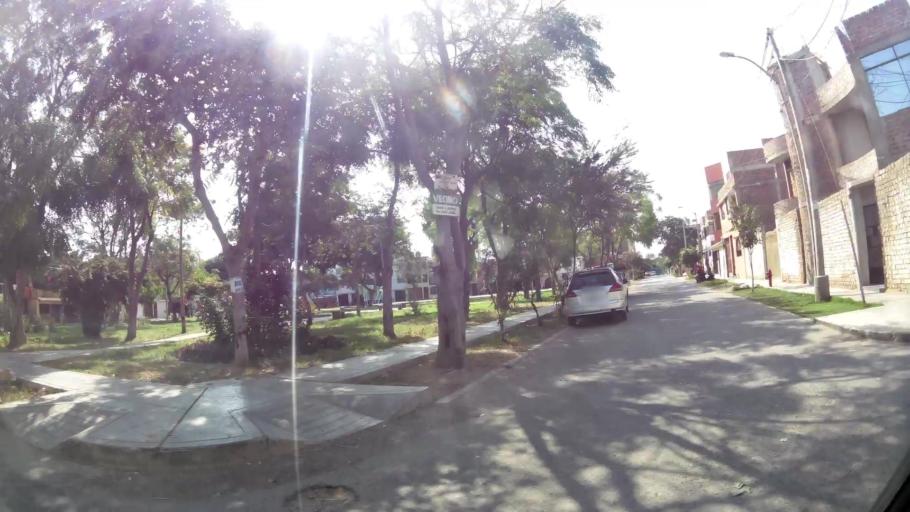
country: PE
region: La Libertad
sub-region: Provincia de Trujillo
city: Trujillo
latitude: -8.1238
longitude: -79.0191
